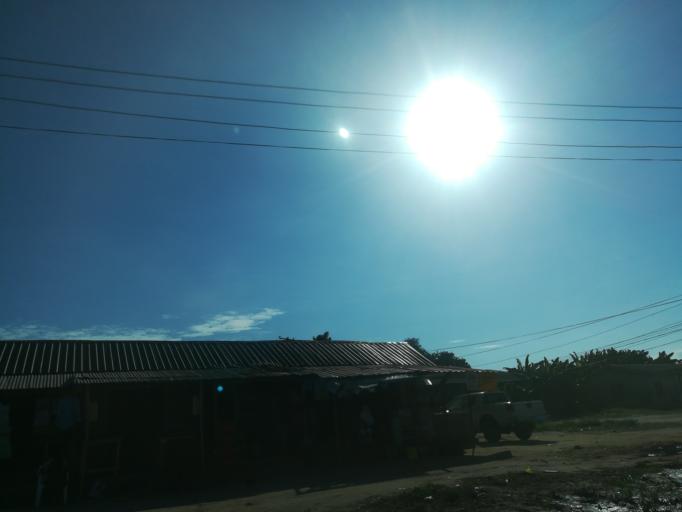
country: NG
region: Lagos
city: Ebute Ikorodu
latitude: 6.5479
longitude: 3.5421
